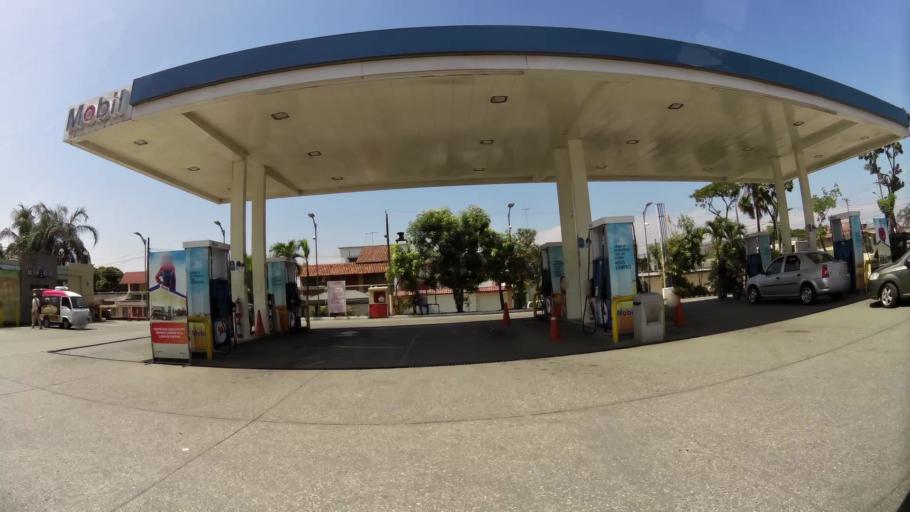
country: EC
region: Guayas
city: Eloy Alfaro
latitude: -2.1137
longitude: -79.9070
